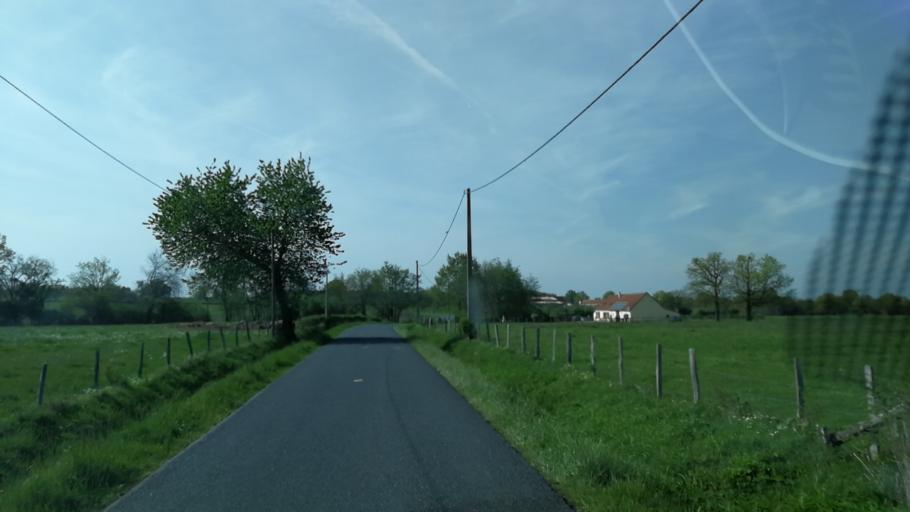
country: FR
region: Auvergne
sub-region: Departement de l'Allier
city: Neuilly-le-Real
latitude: 46.4709
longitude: 3.5314
